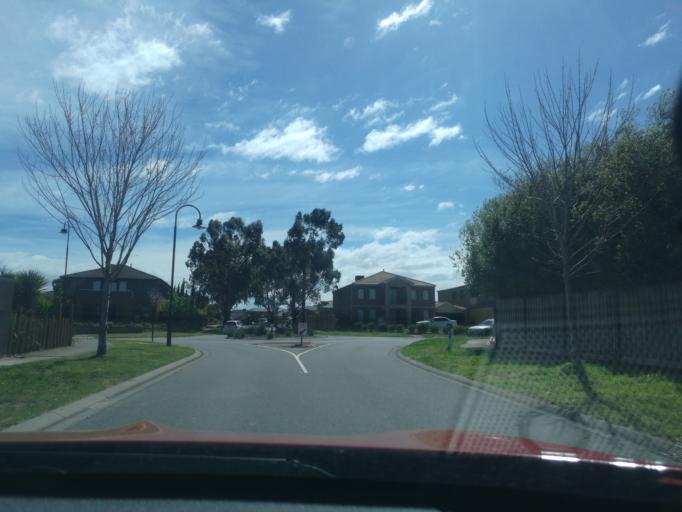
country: AU
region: Victoria
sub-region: Casey
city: Lynbrook
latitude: -38.0660
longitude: 145.2474
